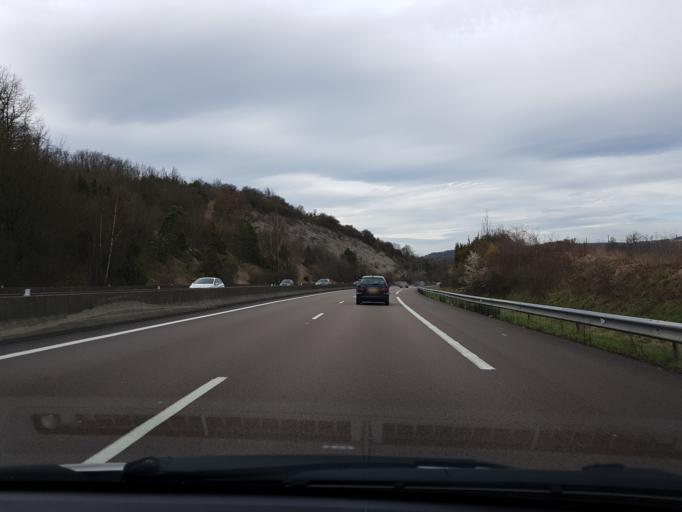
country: FR
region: Bourgogne
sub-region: Departement de la Cote-d'Or
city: Pouilly-en-Auxois
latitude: 47.1789
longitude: 4.6824
